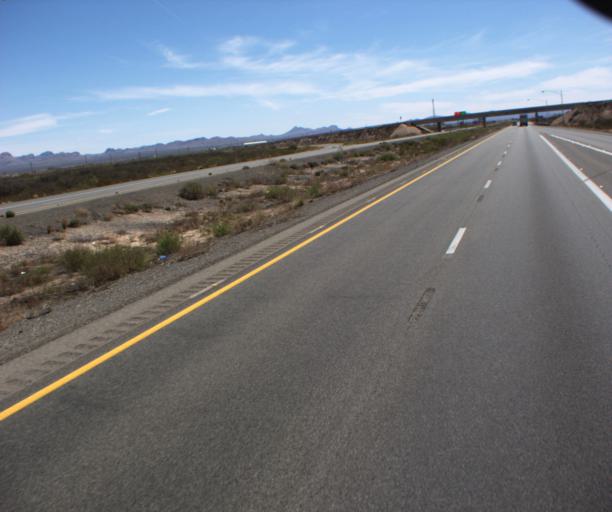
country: US
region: New Mexico
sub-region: Hidalgo County
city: Lordsburg
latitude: 32.2730
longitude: -109.2525
